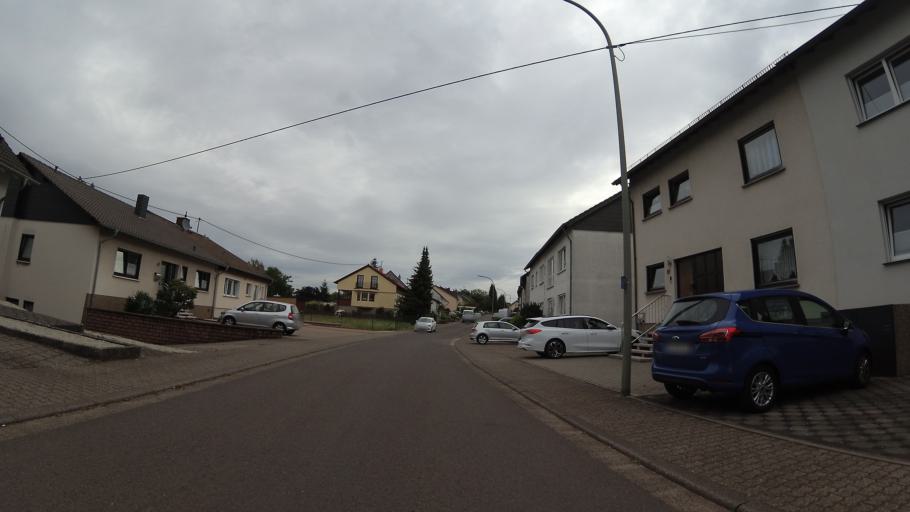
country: DE
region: Saarland
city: Schwalbach
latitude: 49.3146
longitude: 6.8139
